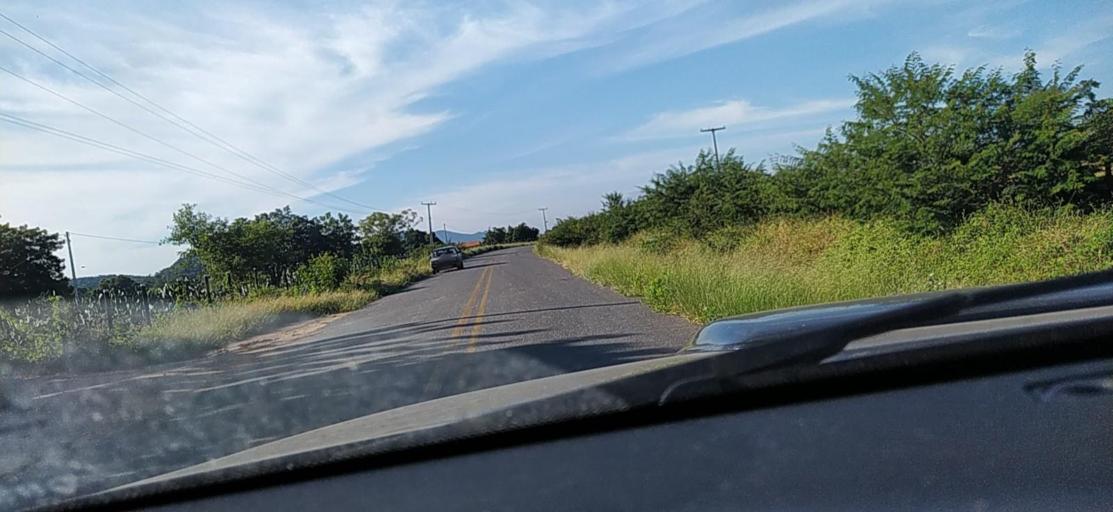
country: BR
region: Bahia
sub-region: Guanambi
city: Guanambi
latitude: -13.9427
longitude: -42.8525
